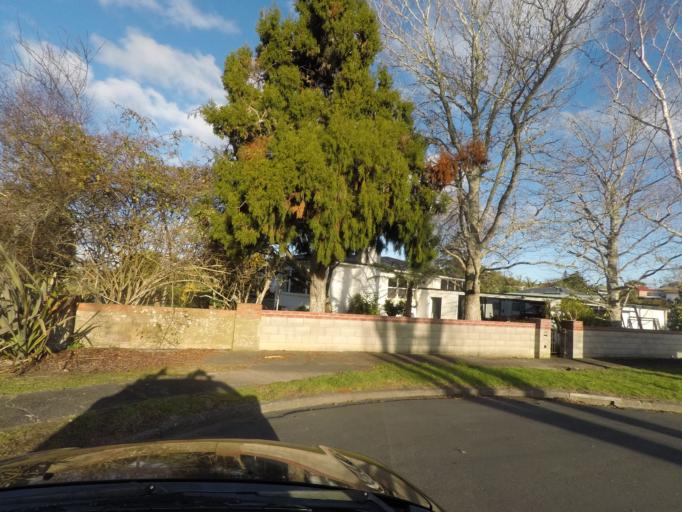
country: NZ
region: Auckland
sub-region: Auckland
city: Waitakere
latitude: -36.8992
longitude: 174.6725
